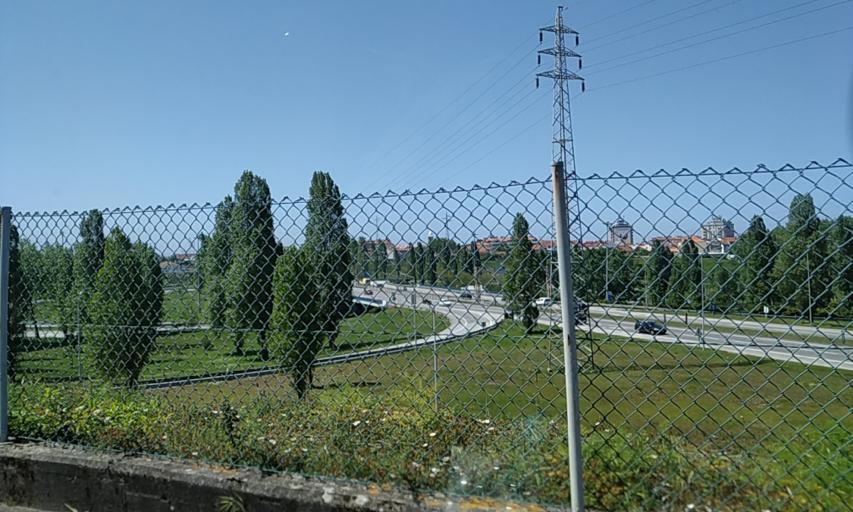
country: PT
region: Aveiro
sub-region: Aveiro
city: Aveiro
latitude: 40.6504
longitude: -8.6219
